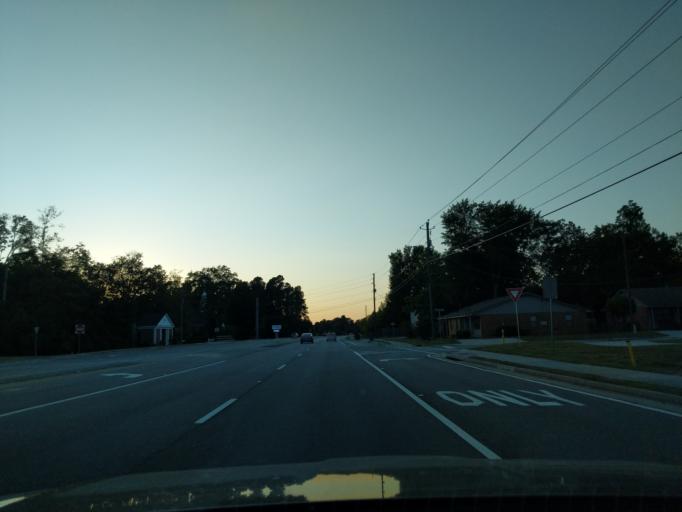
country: US
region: Georgia
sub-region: Columbia County
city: Martinez
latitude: 33.5196
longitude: -82.0816
